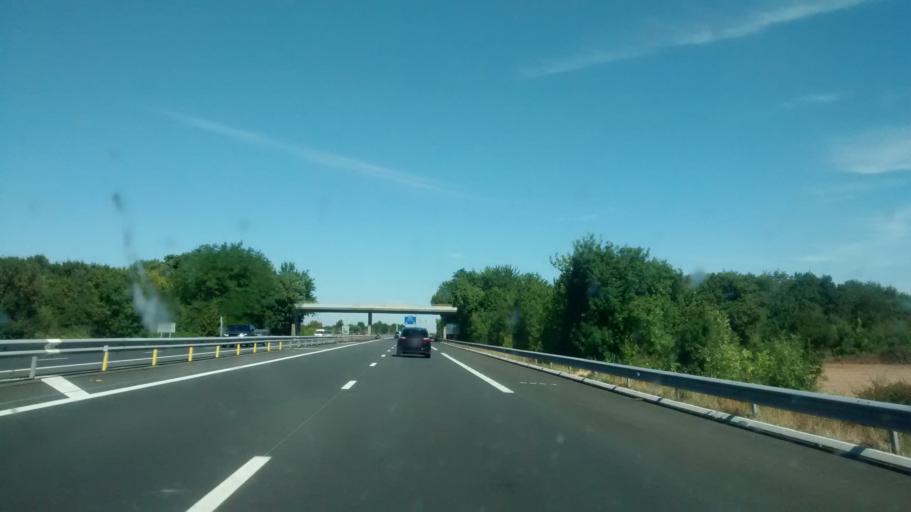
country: FR
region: Poitou-Charentes
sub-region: Departement des Deux-Sevres
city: Fors
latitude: 46.2310
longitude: -0.4418
